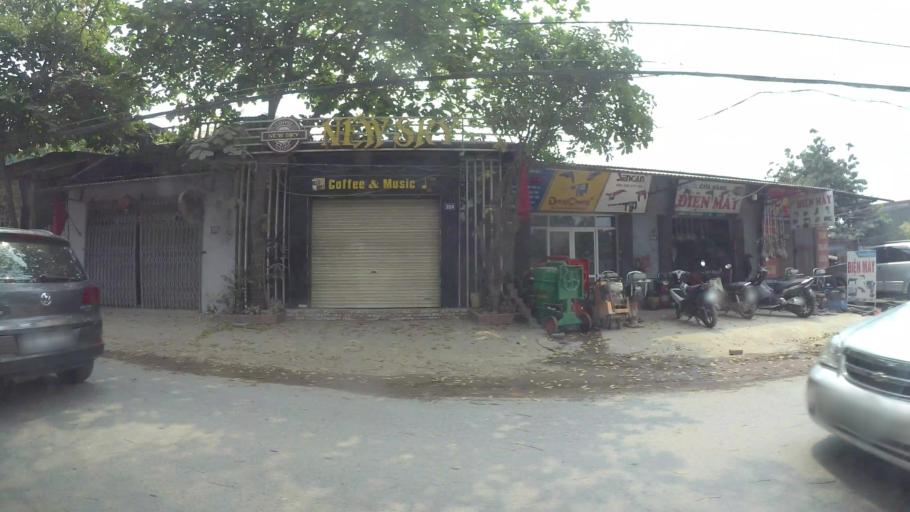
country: VN
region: Ha Noi
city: Cau Dien
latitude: 21.0315
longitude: 105.7393
